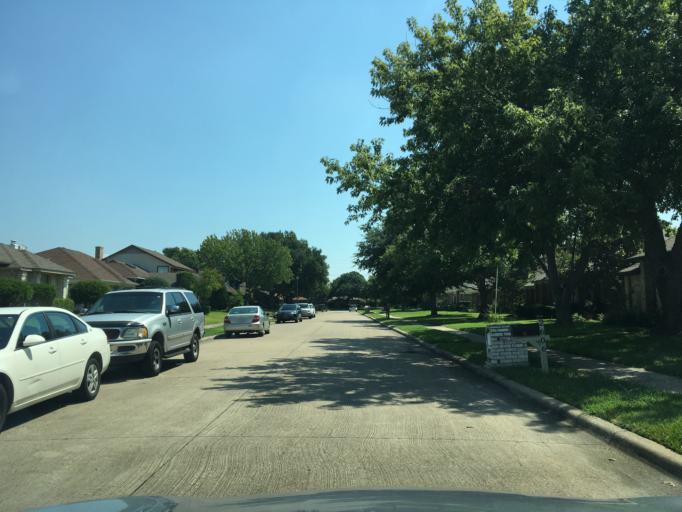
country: US
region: Texas
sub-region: Dallas County
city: Garland
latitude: 32.9420
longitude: -96.6677
